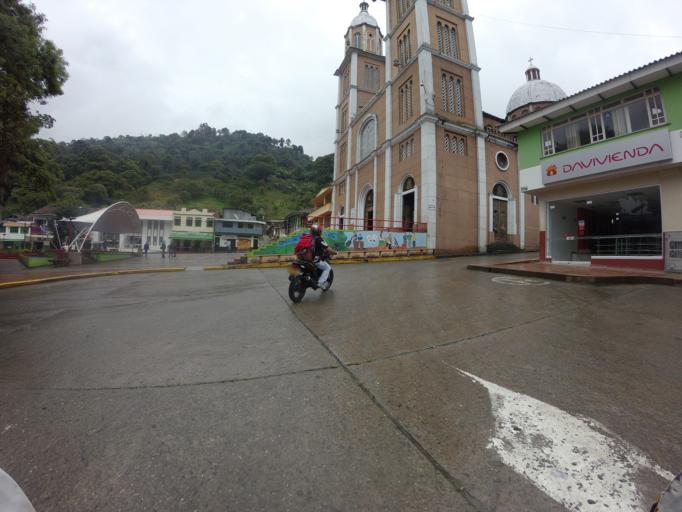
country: CO
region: Quindio
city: Genova
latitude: 4.2066
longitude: -75.7910
